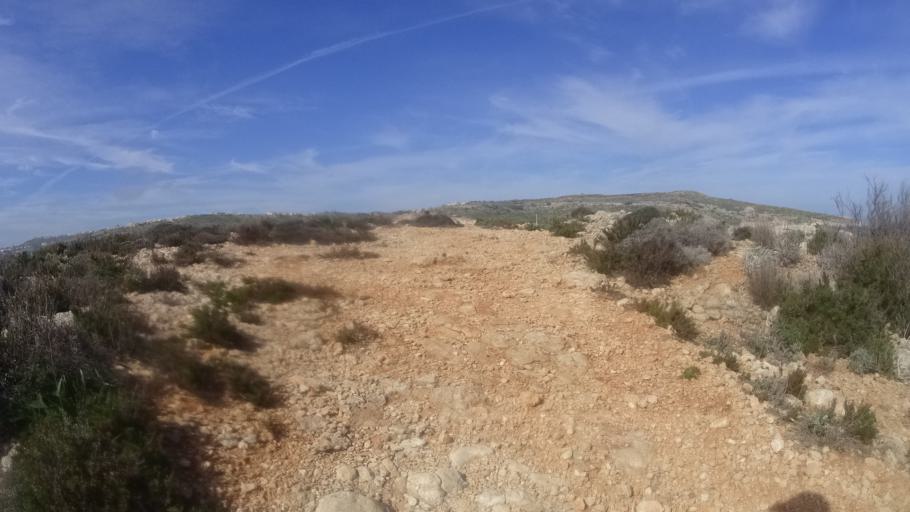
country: MT
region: Il-Qala
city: Qala
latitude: 36.0190
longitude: 14.3285
